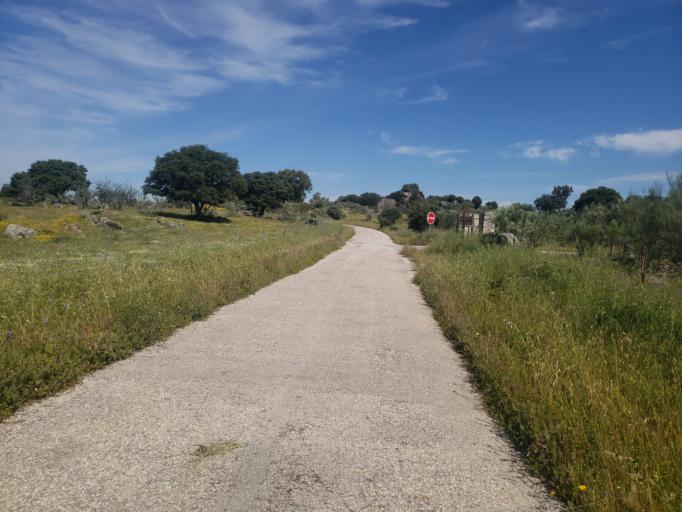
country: ES
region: Extremadura
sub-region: Provincia de Caceres
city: Malpartida de Caceres
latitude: 39.4167
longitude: -6.5014
